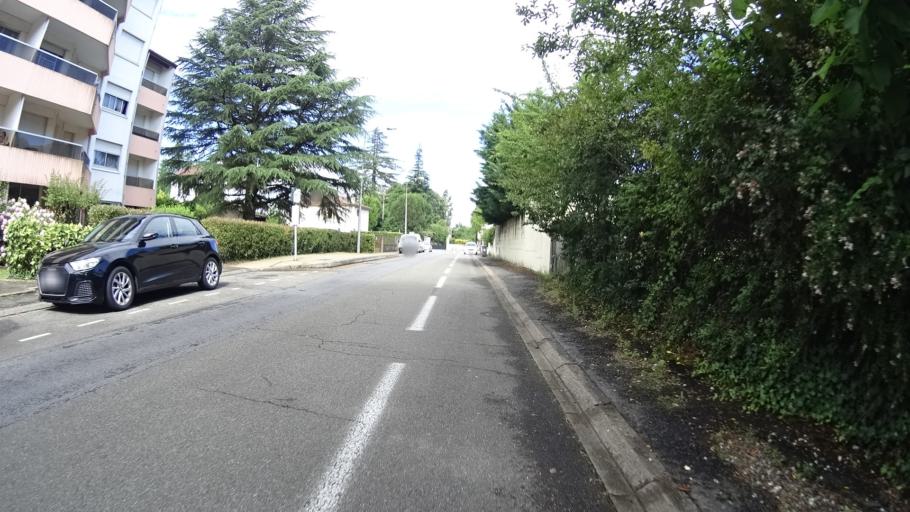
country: FR
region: Aquitaine
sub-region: Departement des Landes
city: Dax
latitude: 43.7032
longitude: -1.0613
